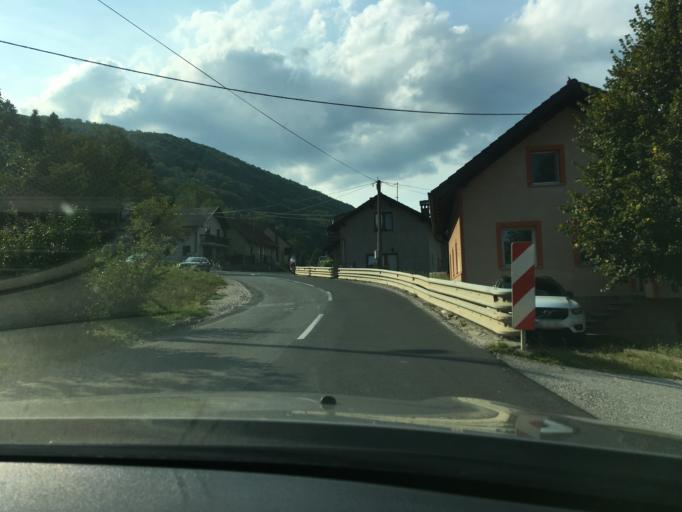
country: SI
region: Dolenjske Toplice
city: Dolenjske Toplice
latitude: 45.7608
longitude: 15.0305
